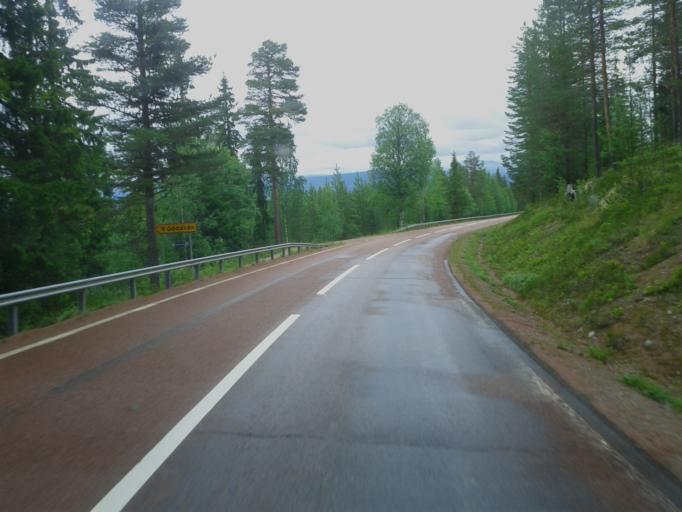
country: NO
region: Hedmark
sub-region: Trysil
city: Innbygda
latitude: 61.8513
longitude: 12.6148
